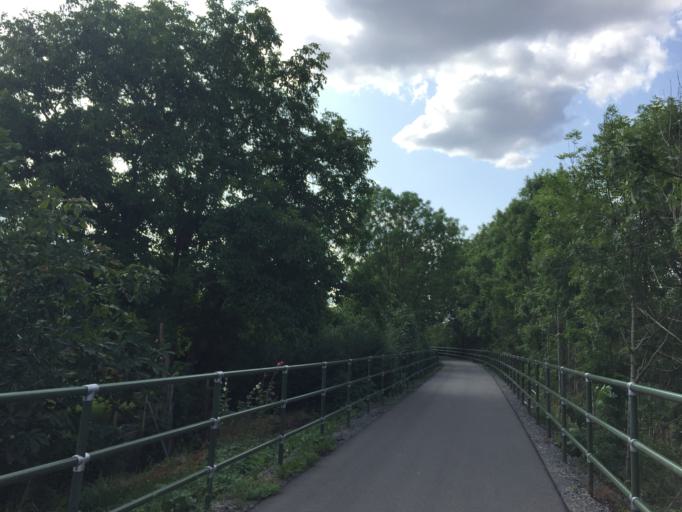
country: DE
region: Hesse
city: Schwalmstadt
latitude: 50.9122
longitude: 9.1968
